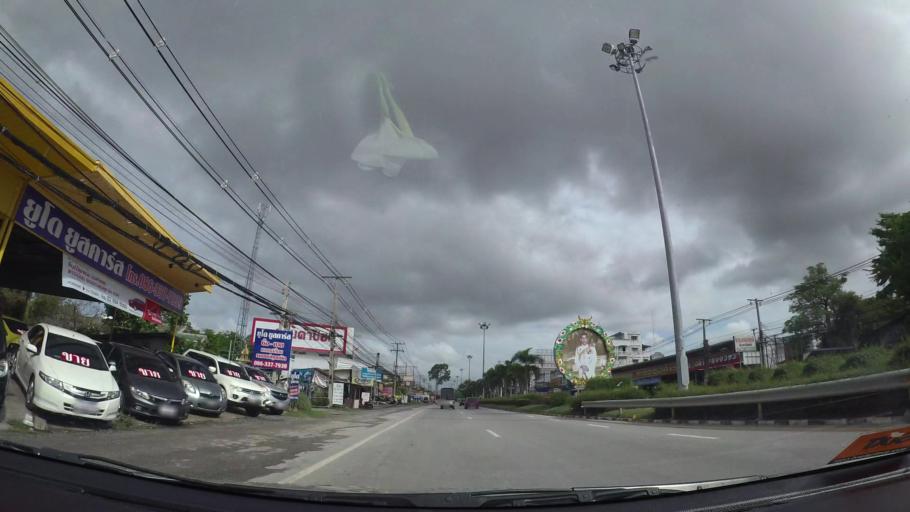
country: TH
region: Rayong
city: Rayong
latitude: 12.6911
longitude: 101.2056
